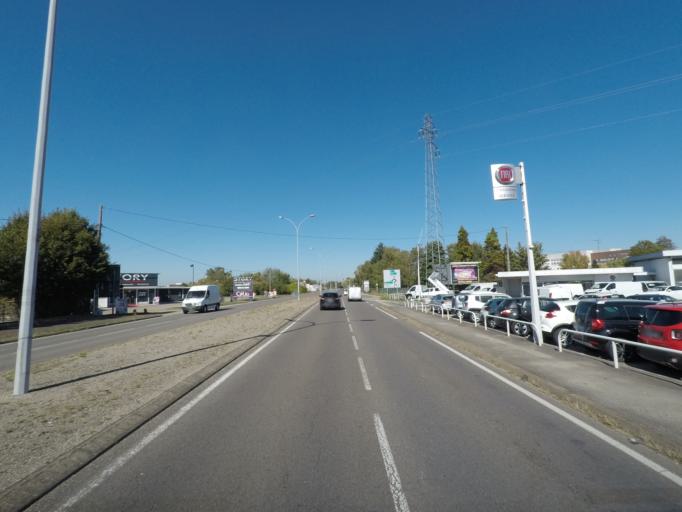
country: FR
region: Rhone-Alpes
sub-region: Departement de l'Ain
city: Bourg-en-Bresse
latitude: 46.2203
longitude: 5.2106
